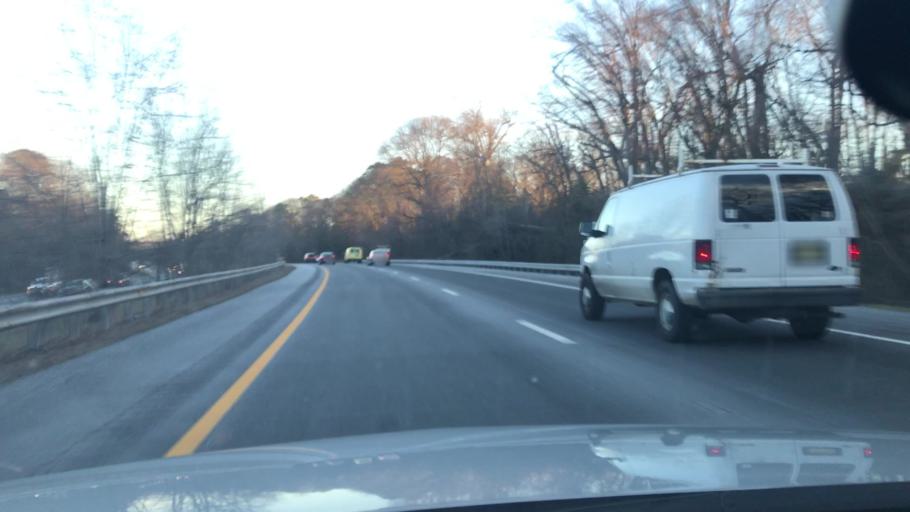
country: US
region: New Jersey
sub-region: Gloucester County
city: Turnersville
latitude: 39.7594
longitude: -75.0416
